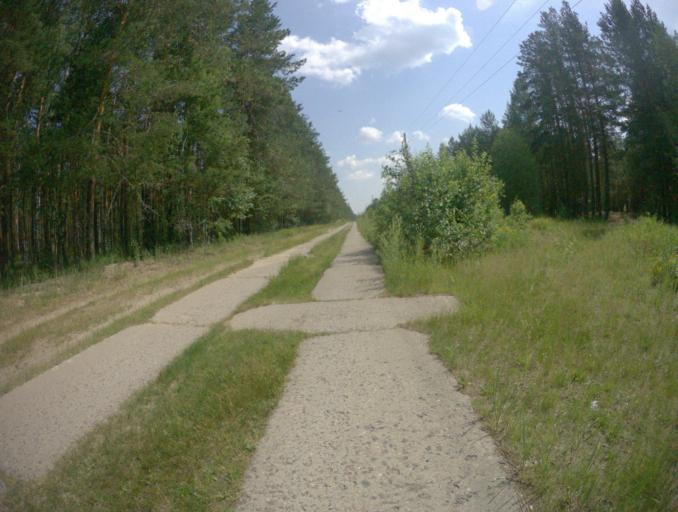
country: RU
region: Nizjnij Novgorod
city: Frolishchi
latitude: 56.4059
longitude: 42.4884
